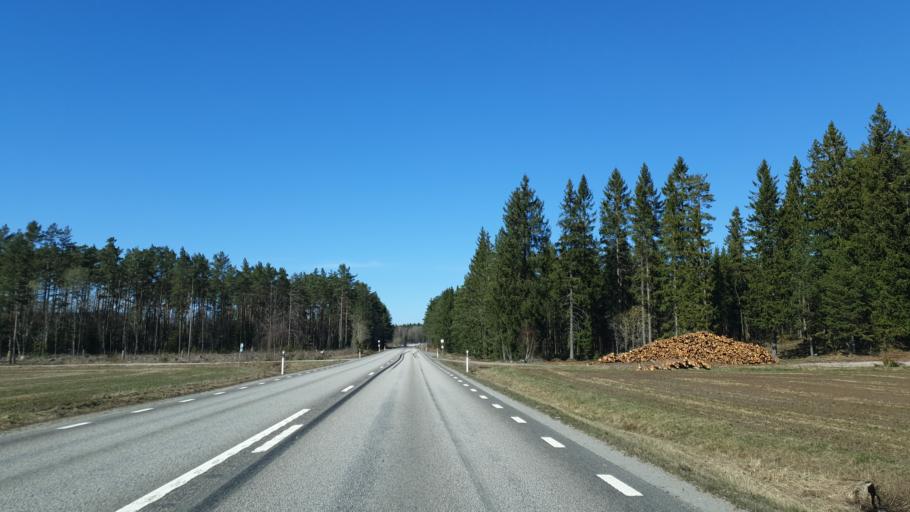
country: SE
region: Vaestra Goetaland
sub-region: Svenljunga Kommun
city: Svenljunga
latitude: 57.4642
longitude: 13.1134
